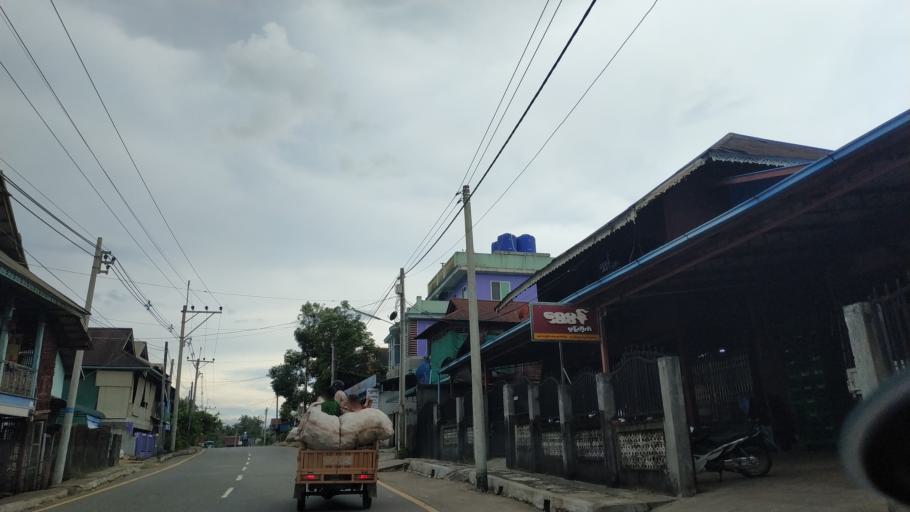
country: MM
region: Tanintharyi
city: Dawei
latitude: 14.0721
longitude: 98.2109
